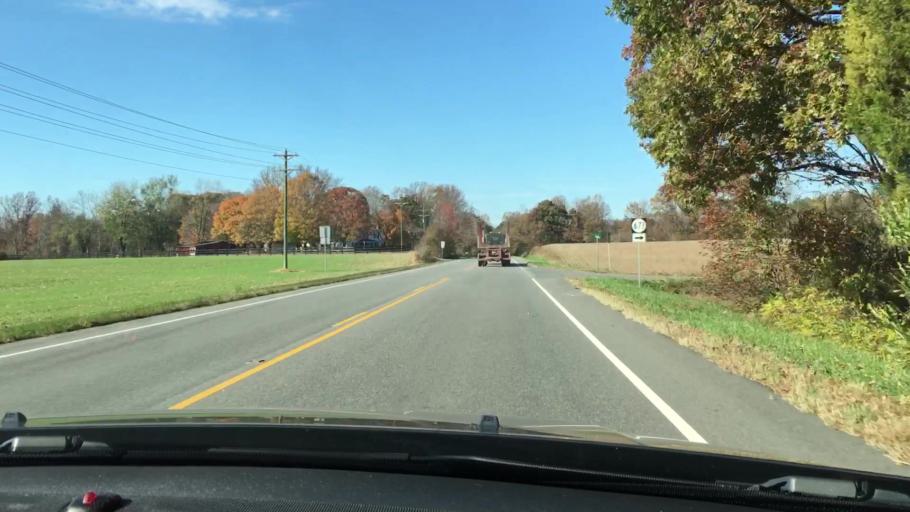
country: US
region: Virginia
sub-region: Hanover County
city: Hanover
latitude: 37.8036
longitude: -77.2639
